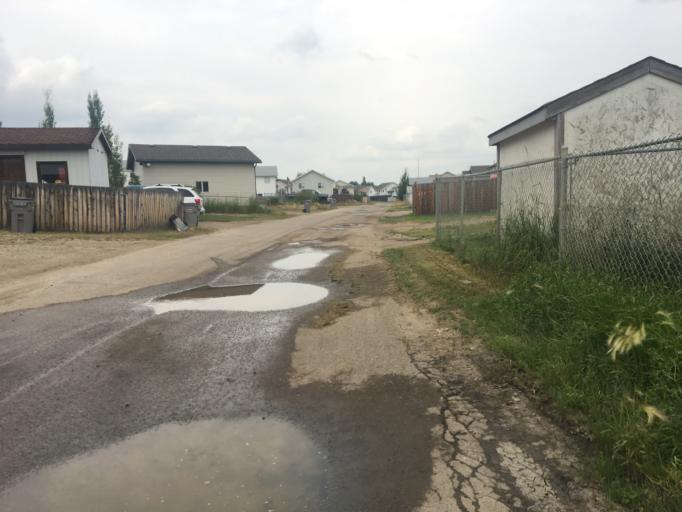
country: CA
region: Alberta
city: Grande Prairie
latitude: 55.1463
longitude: -118.8118
